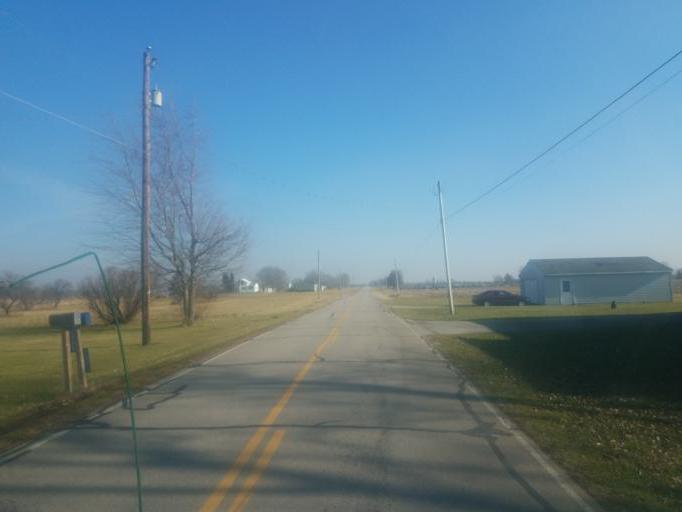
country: US
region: Ohio
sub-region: Crawford County
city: Bucyrus
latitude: 40.9069
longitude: -83.0115
